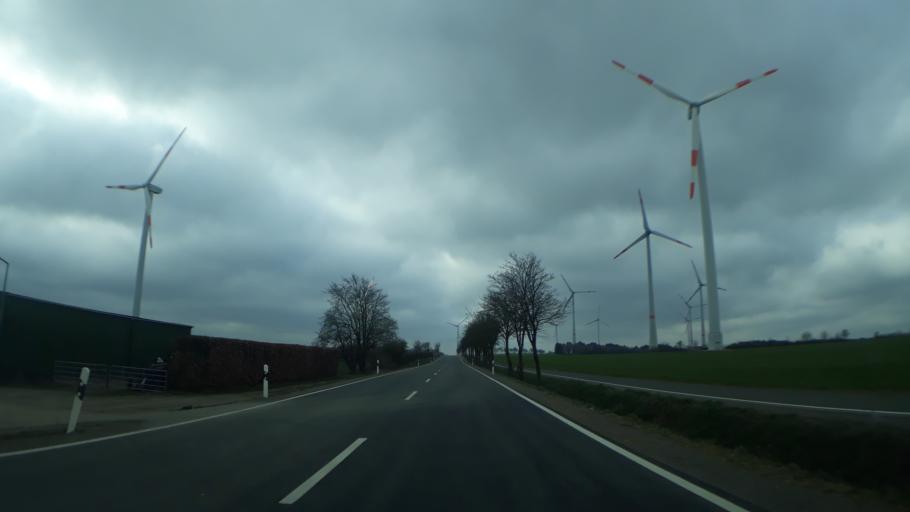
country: DE
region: North Rhine-Westphalia
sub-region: Regierungsbezirk Koln
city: Hellenthal
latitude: 50.5230
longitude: 6.3805
